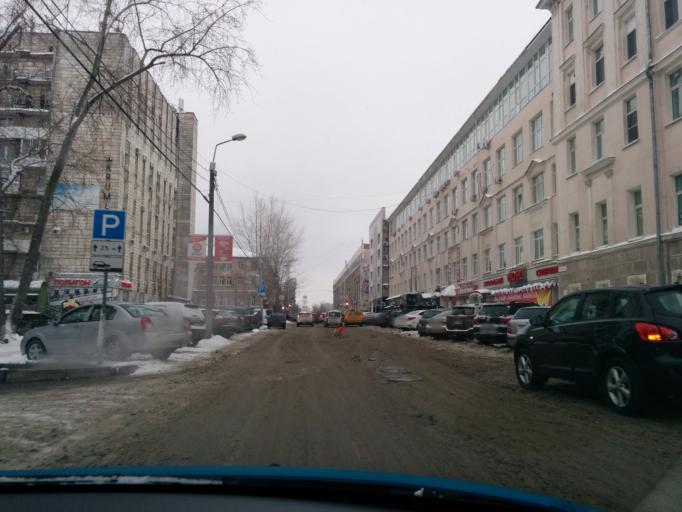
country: RU
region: Perm
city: Perm
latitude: 58.0154
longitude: 56.2334
